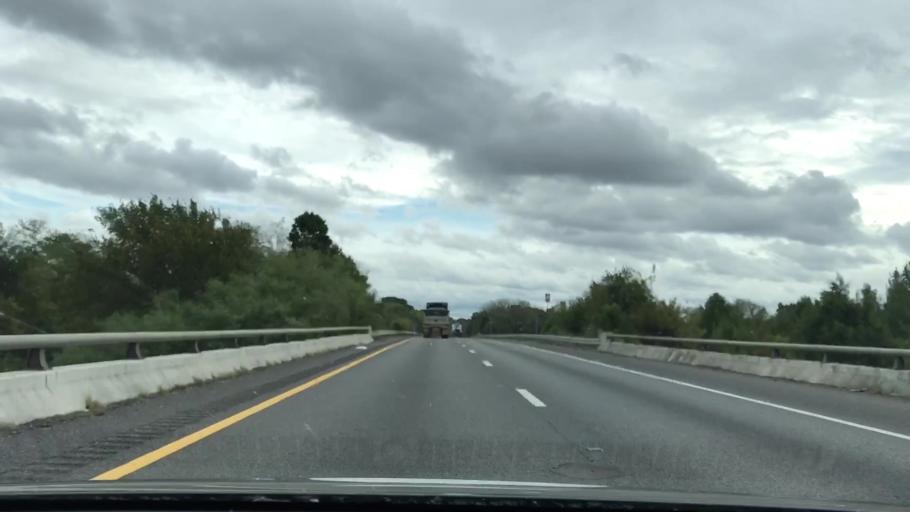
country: US
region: Kentucky
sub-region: Todd County
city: Guthrie
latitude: 36.5253
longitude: -87.2218
